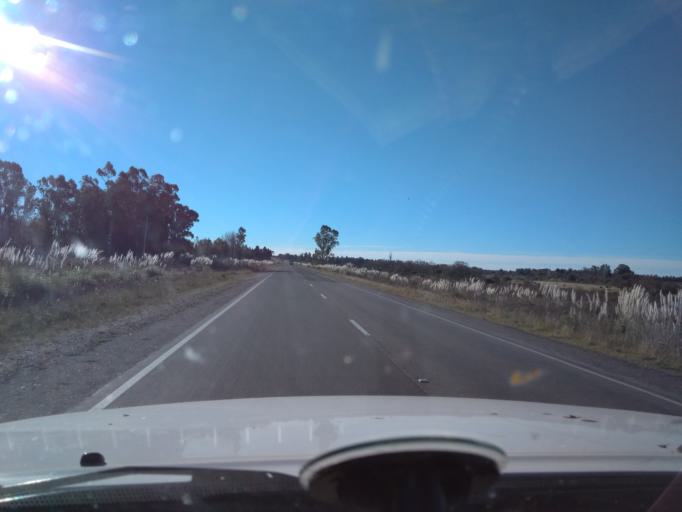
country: UY
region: Canelones
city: Sauce
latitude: -34.6041
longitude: -56.0492
